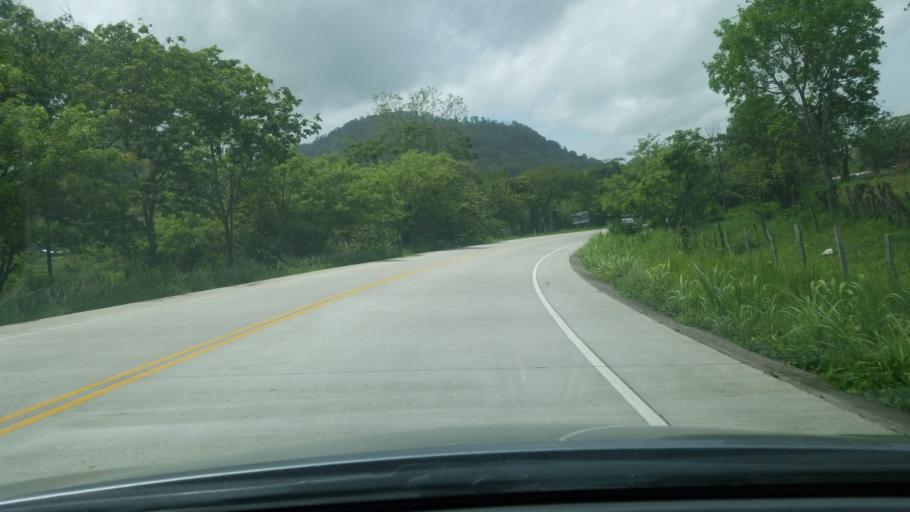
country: HN
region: Copan
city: Trinidad de Copan
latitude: 14.9525
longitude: -88.7670
